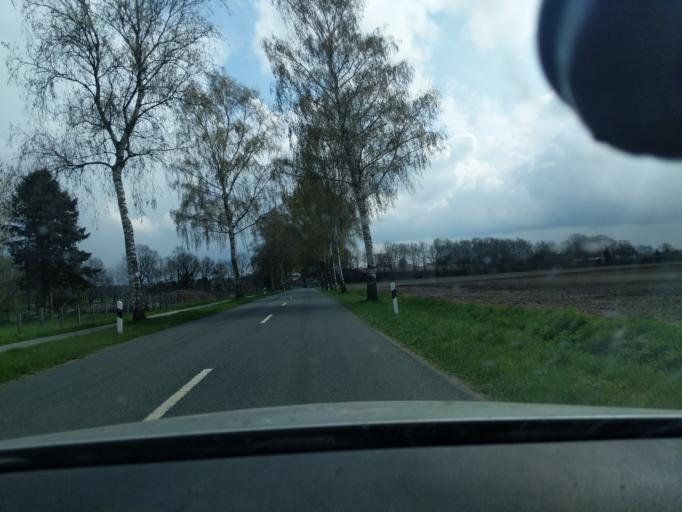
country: DE
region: Lower Saxony
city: Deinste
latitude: 53.5294
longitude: 9.4776
